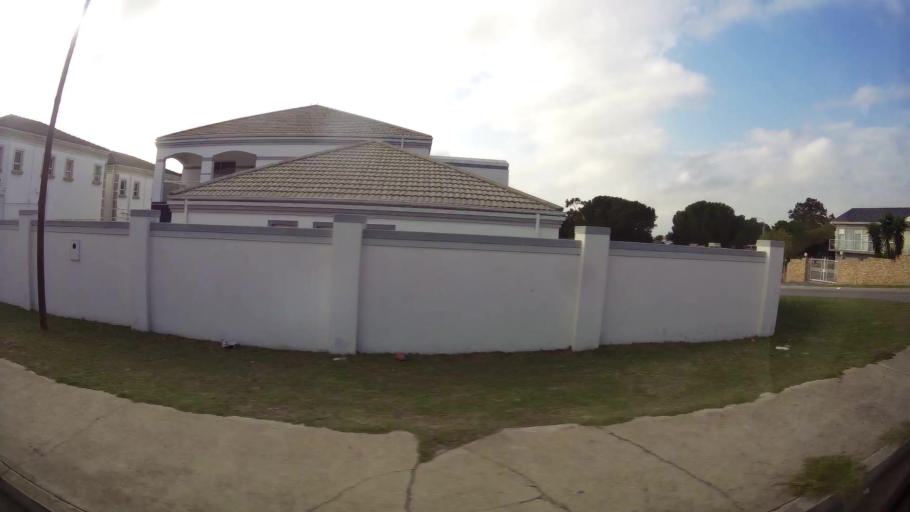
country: ZA
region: Eastern Cape
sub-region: Nelson Mandela Bay Metropolitan Municipality
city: Port Elizabeth
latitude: -33.9247
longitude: 25.5547
